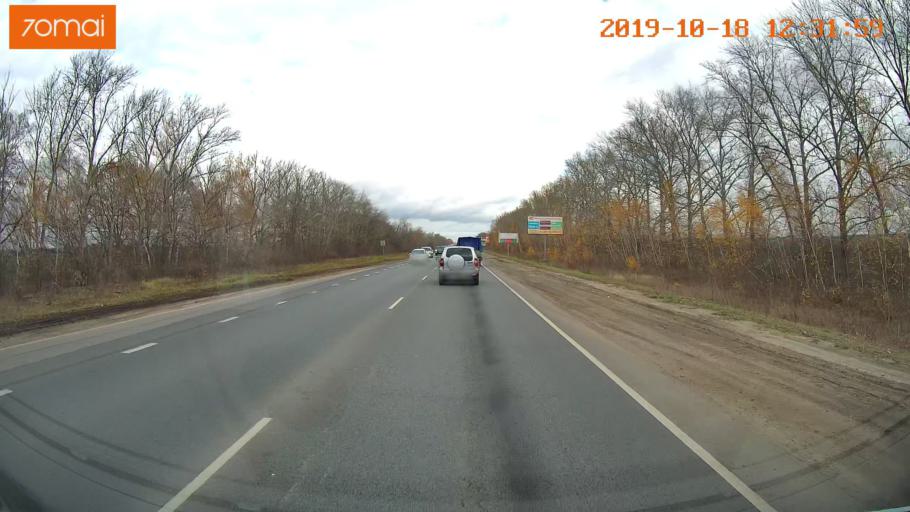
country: RU
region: Rjazan
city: Ryazan'
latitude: 54.5976
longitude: 39.6196
